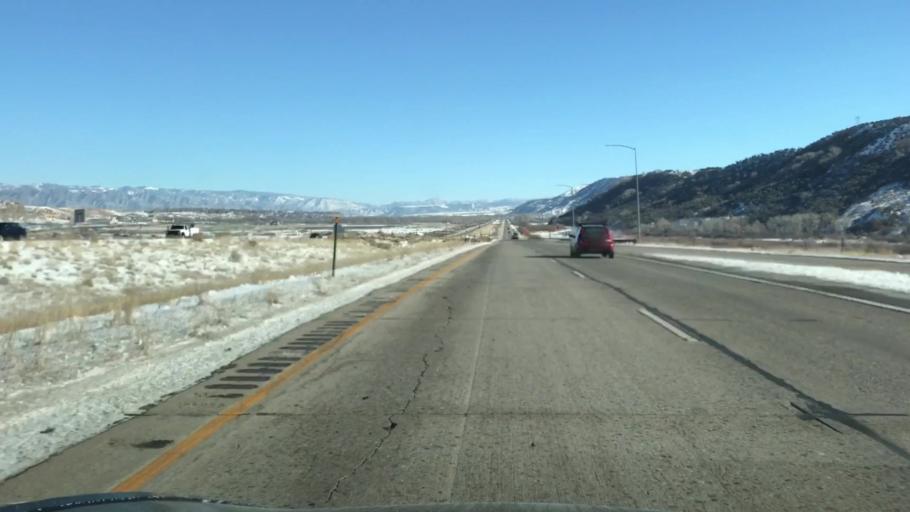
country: US
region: Colorado
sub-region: Garfield County
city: Rifle
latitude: 39.5202
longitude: -107.8405
